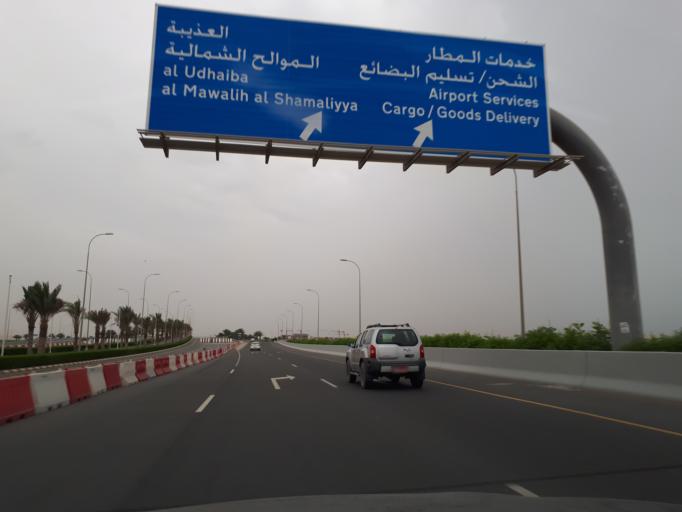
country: OM
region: Muhafazat Masqat
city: Bawshar
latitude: 23.6036
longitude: 58.3184
